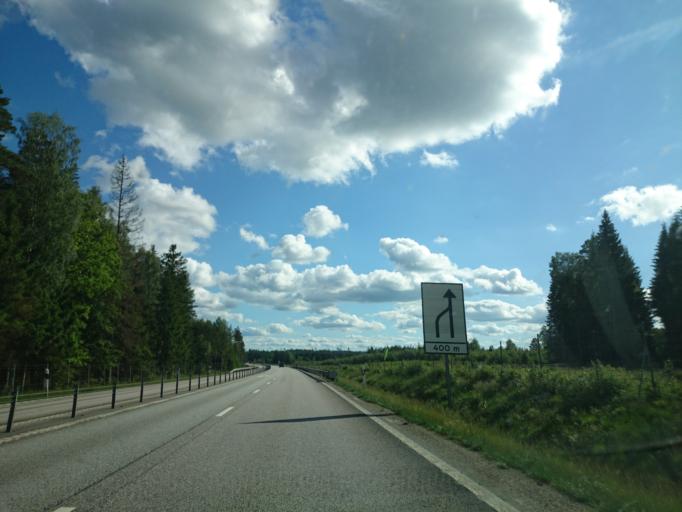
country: SE
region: Kronoberg
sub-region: Ljungby Kommun
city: Lagan
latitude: 56.8934
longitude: 13.9582
